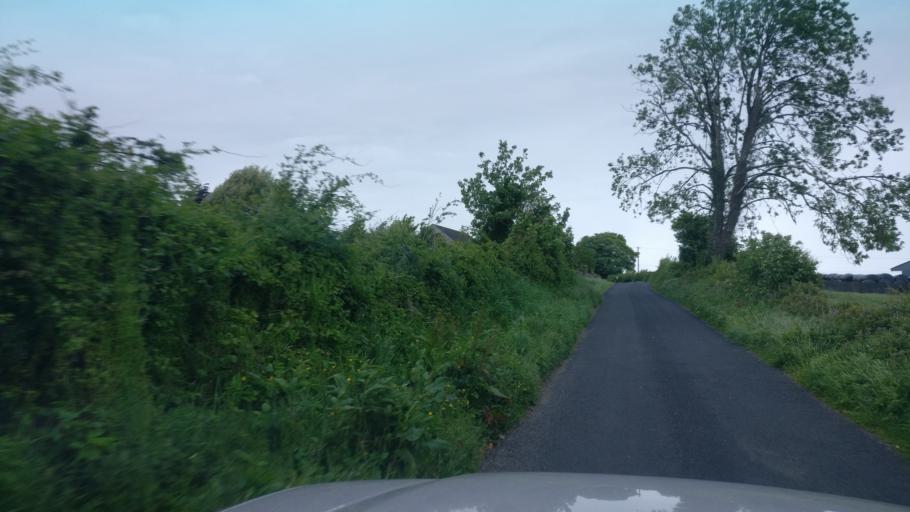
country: IE
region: Connaught
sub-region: County Galway
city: Loughrea
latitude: 53.1176
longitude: -8.4338
